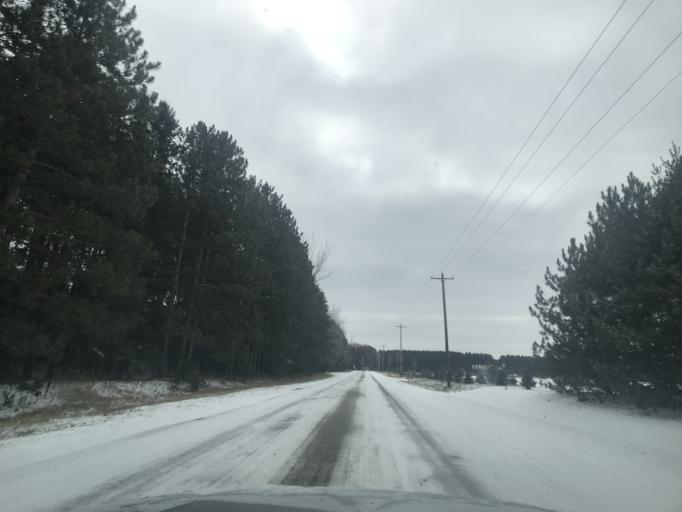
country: US
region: Wisconsin
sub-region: Brown County
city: Suamico
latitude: 44.6943
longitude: -88.1008
